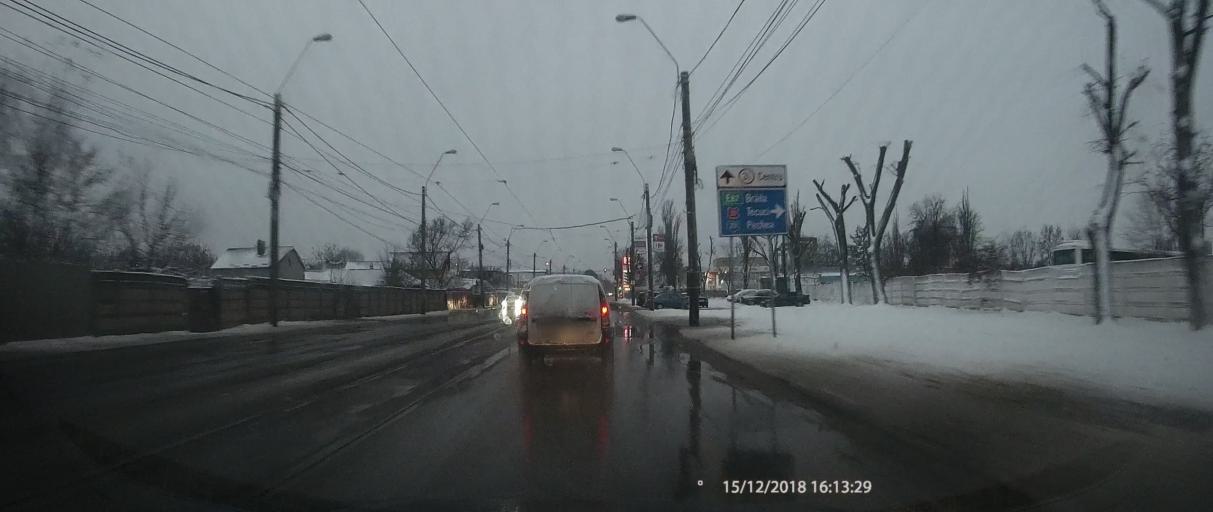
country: RO
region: Galati
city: Galati
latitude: 45.4631
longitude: 28.0337
